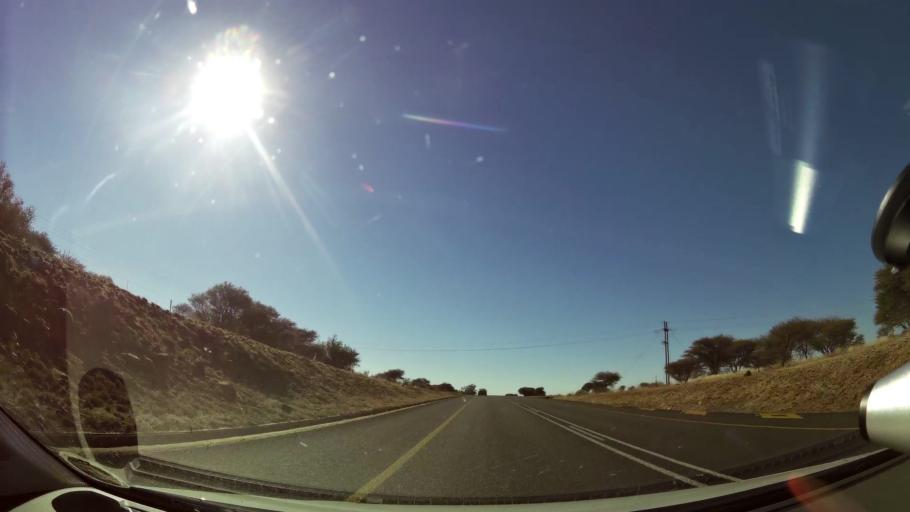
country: ZA
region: Northern Cape
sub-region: Frances Baard District Municipality
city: Warrenton
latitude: -28.0823
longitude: 24.8775
